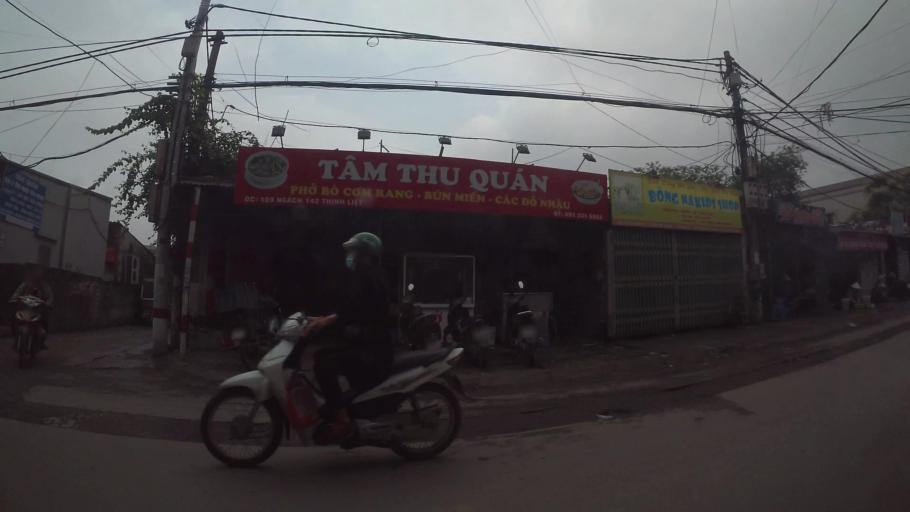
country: VN
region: Ha Noi
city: Van Dien
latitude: 20.9723
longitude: 105.8475
